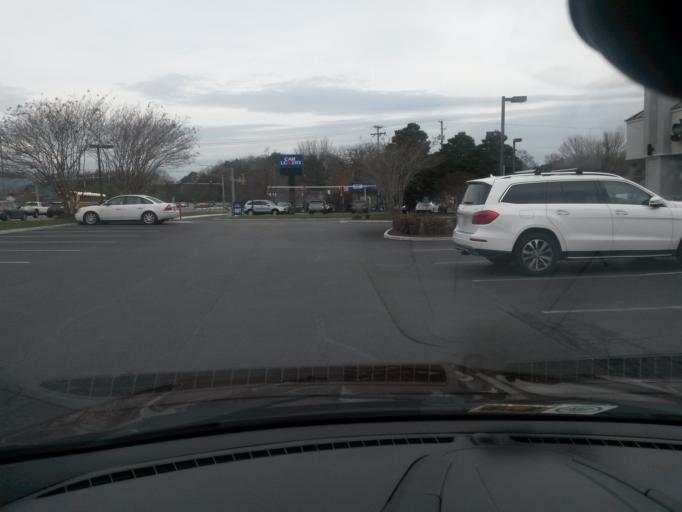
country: US
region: Virginia
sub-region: Roanoke County
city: Cave Spring
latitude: 37.2269
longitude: -79.9985
